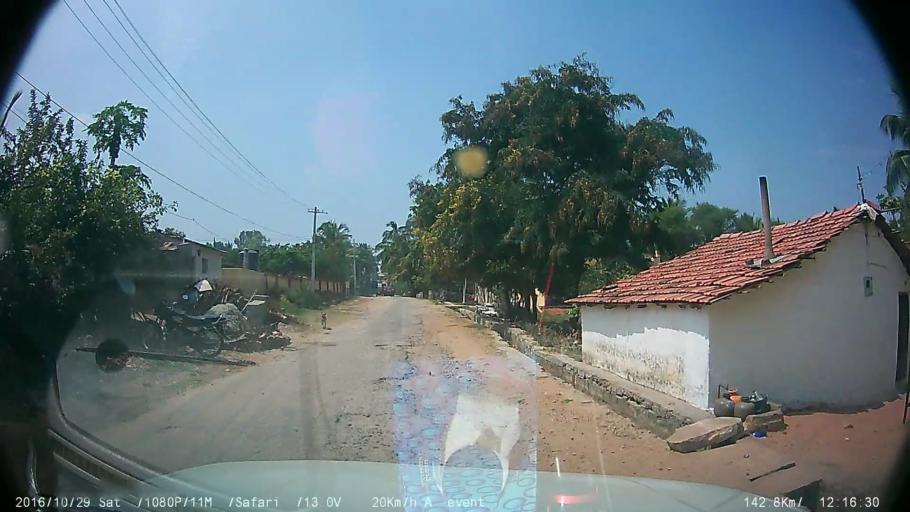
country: IN
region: Karnataka
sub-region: Mysore
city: Mysore
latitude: 12.3781
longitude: 76.5853
